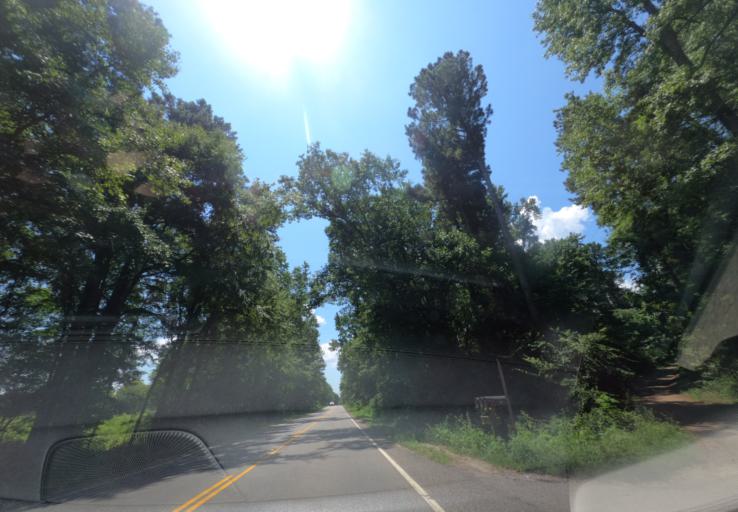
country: US
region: South Carolina
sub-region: Aiken County
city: Belvedere
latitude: 33.5597
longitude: -82.0098
